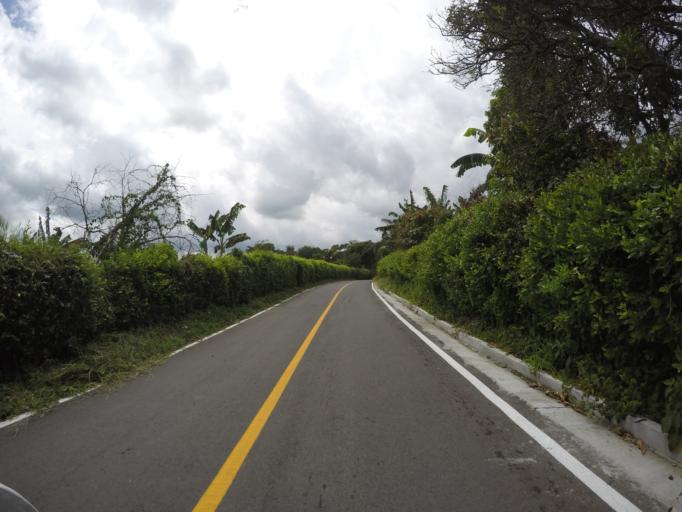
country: CO
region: Quindio
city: Quimbaya
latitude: 4.6127
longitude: -75.7540
